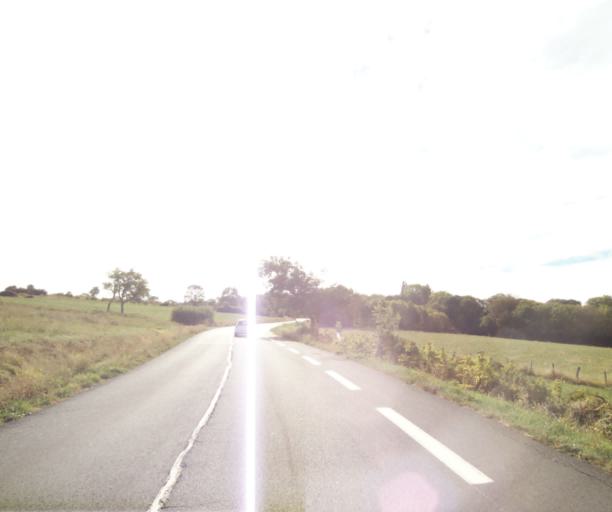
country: FR
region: Auvergne
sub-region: Departement du Puy-de-Dome
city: Romagnat
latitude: 45.7157
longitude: 3.0904
